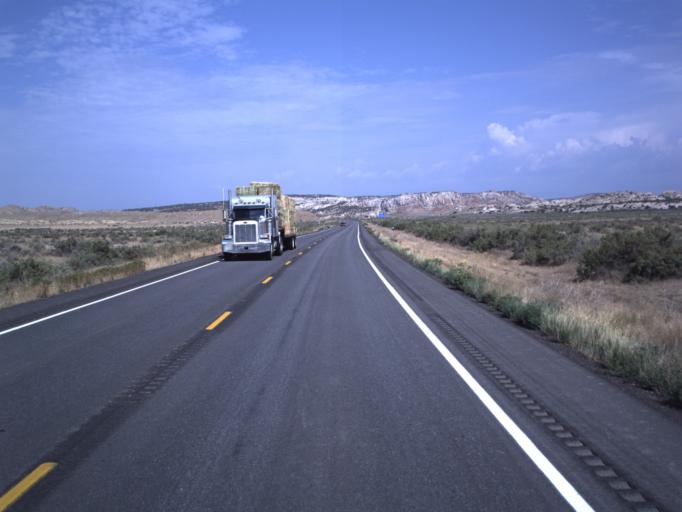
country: US
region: Utah
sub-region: Uintah County
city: Naples
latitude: 40.3103
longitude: -109.2204
